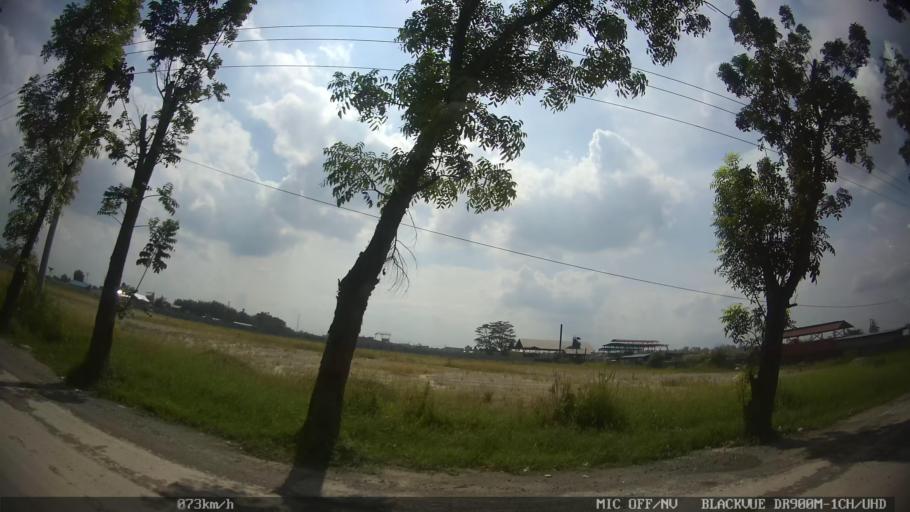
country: ID
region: North Sumatra
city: Binjai
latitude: 3.6297
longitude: 98.5349
